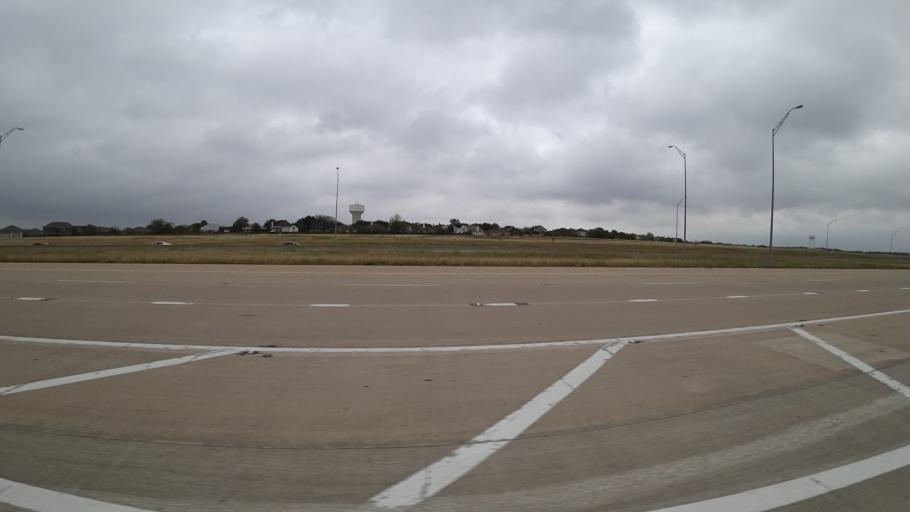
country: US
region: Texas
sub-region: Travis County
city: Windemere
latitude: 30.4862
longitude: -97.6206
